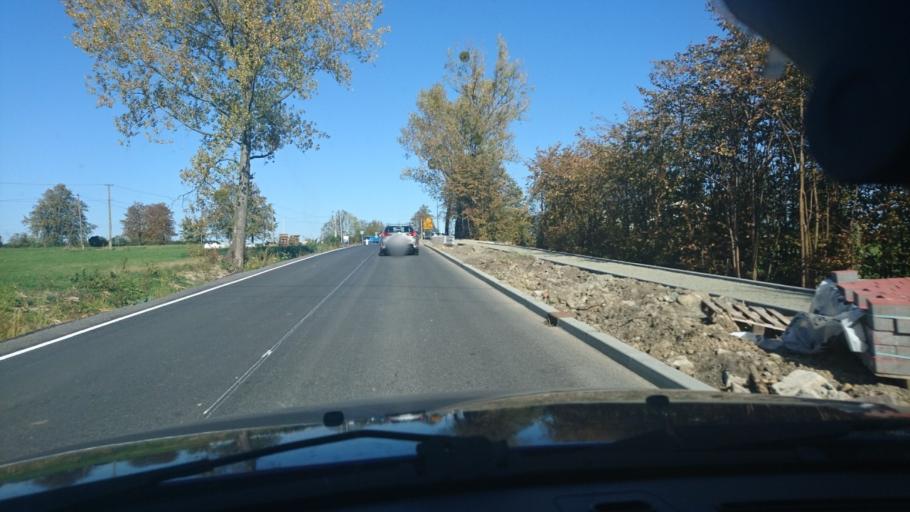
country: PL
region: Silesian Voivodeship
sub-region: Powiat bielski
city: Bronow
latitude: 49.8557
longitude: 18.8956
